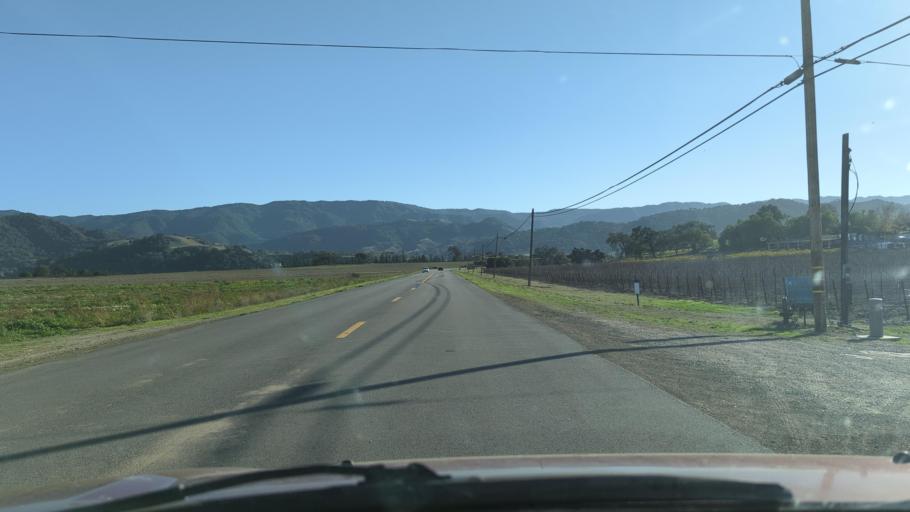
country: US
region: California
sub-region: Santa Barbara County
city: Santa Ynez
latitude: 34.5964
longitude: -120.0982
